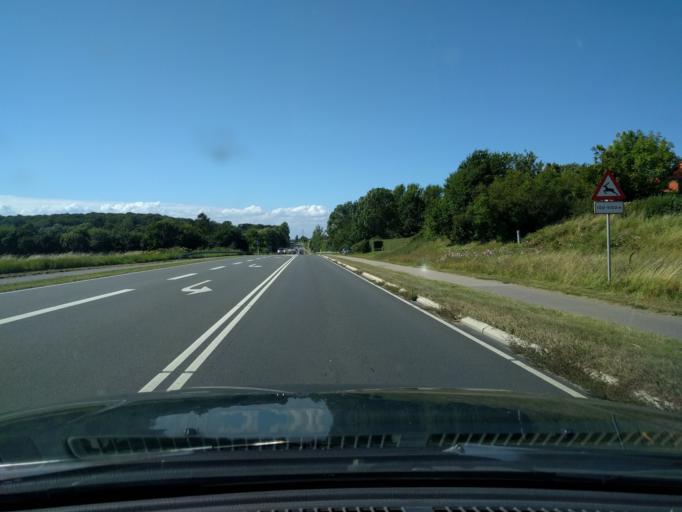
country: DK
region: Zealand
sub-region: Slagelse Kommune
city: Korsor
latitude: 55.3230
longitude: 11.1935
